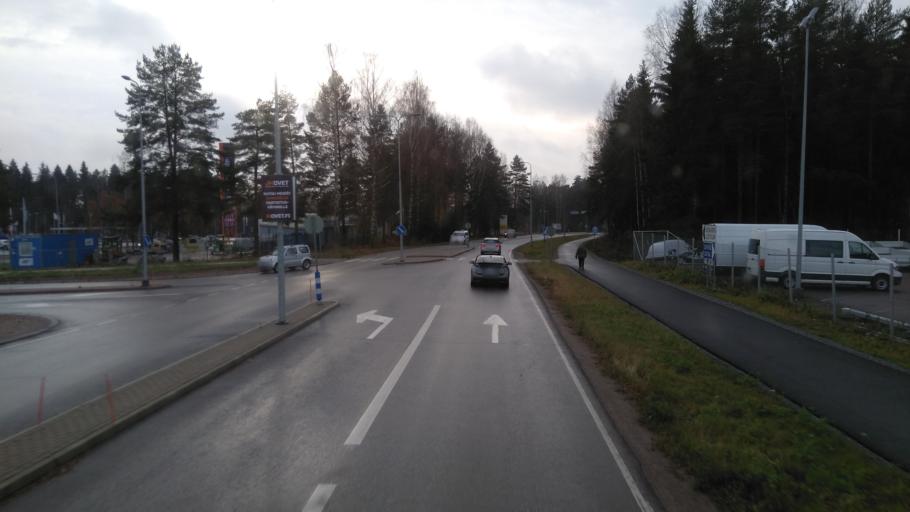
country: FI
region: Uusimaa
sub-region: Porvoo
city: Porvoo
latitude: 60.4009
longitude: 25.6854
